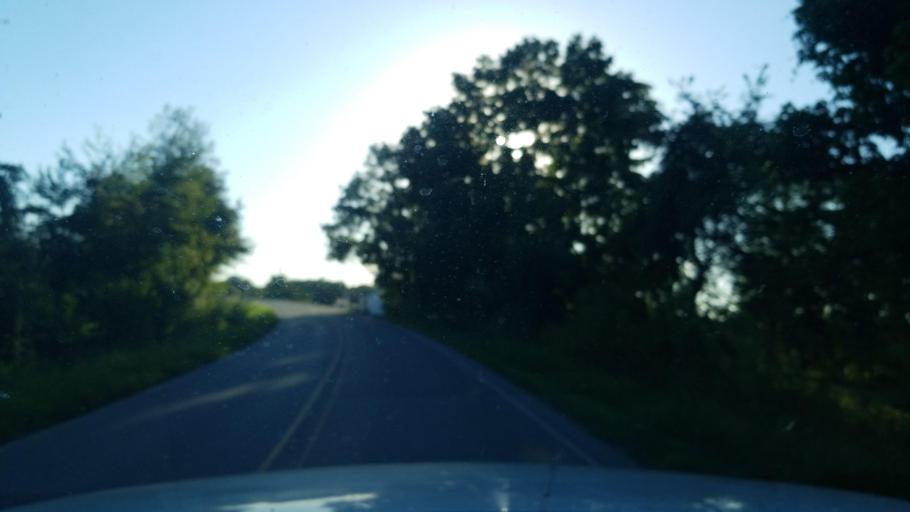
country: US
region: Illinois
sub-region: Hardin County
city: Elizabethtown
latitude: 37.5737
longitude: -88.3941
